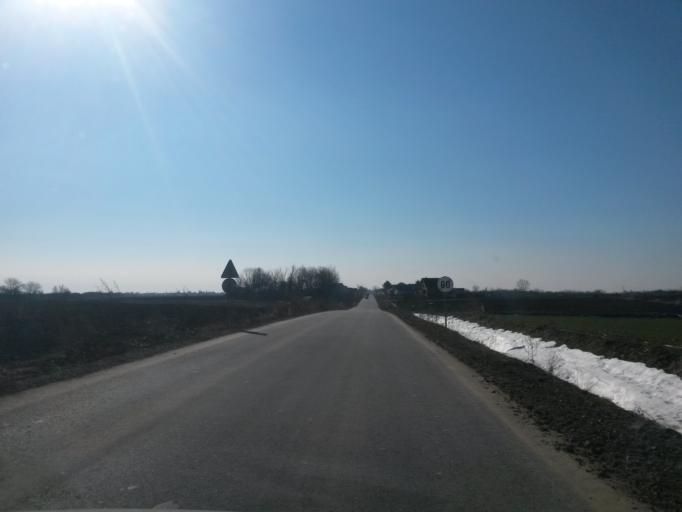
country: HR
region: Vukovarsko-Srijemska
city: Negoslavci
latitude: 45.2964
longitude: 19.0032
